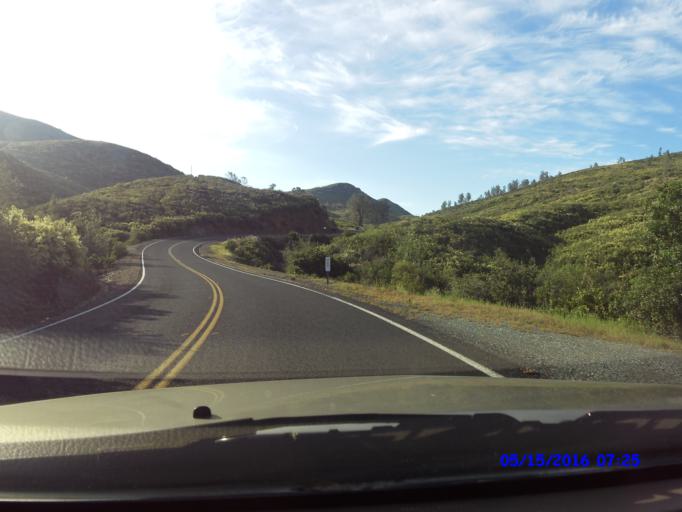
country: US
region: California
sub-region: Tuolumne County
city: Tuolumne City
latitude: 37.7600
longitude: -120.2533
